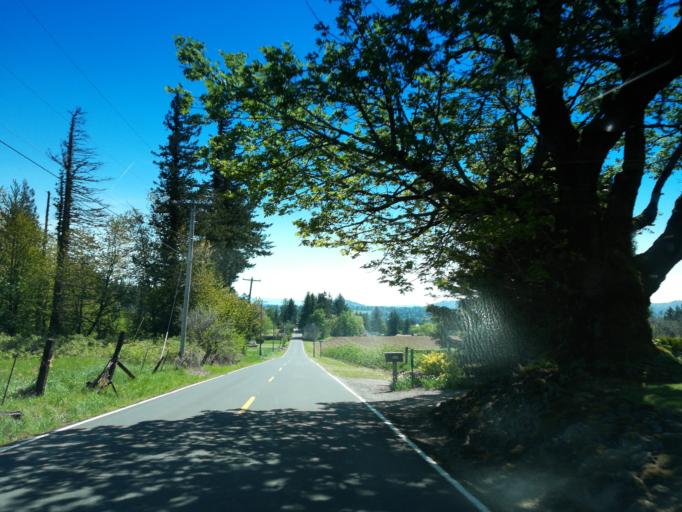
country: US
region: Oregon
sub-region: Multnomah County
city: Troutdale
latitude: 45.5269
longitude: -122.3523
